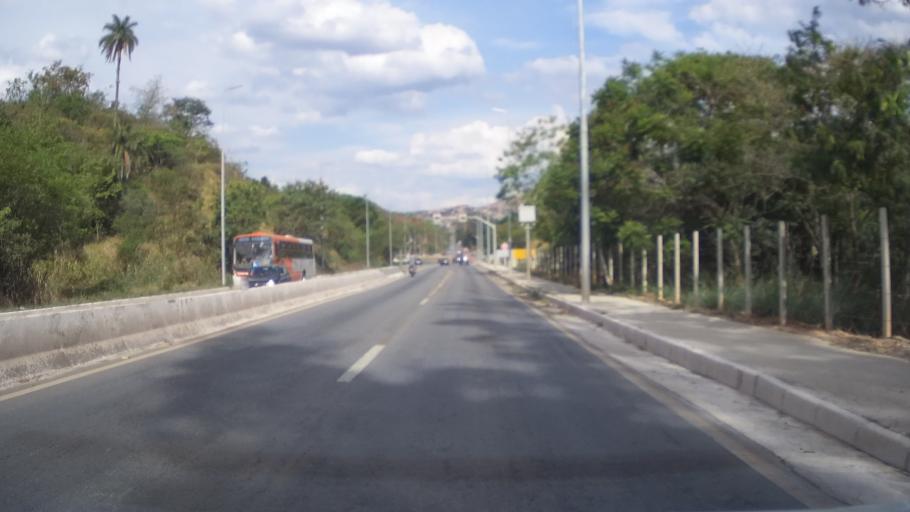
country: BR
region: Minas Gerais
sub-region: Belo Horizonte
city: Belo Horizonte
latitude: -19.8747
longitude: -43.8773
